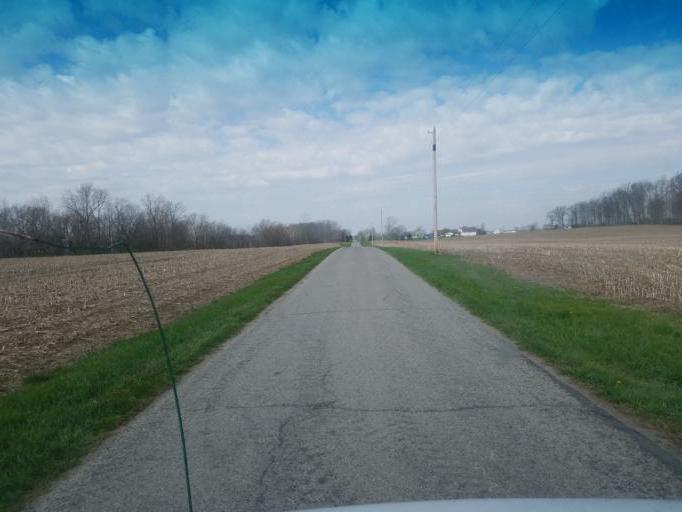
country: US
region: Ohio
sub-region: Logan County
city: Northwood
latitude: 40.4919
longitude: -83.7234
